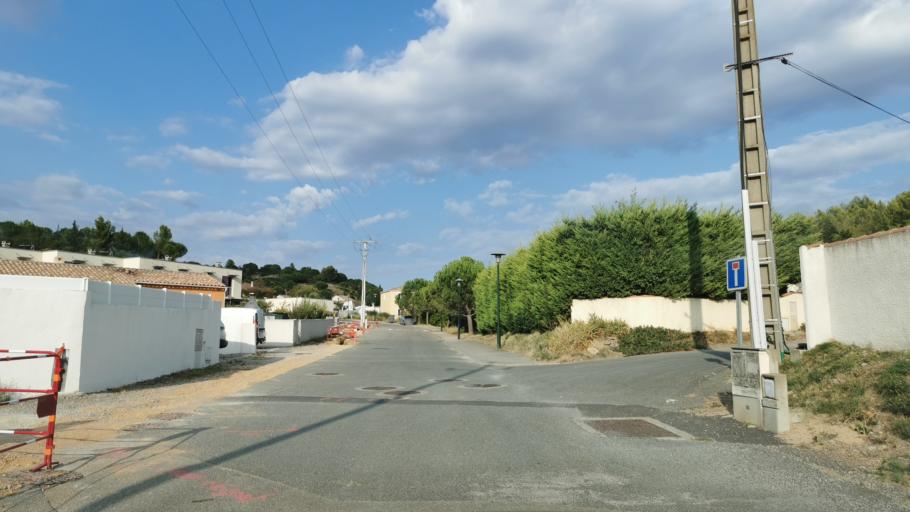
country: FR
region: Languedoc-Roussillon
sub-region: Departement de l'Aude
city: Bizanet
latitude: 43.1677
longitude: 2.8806
